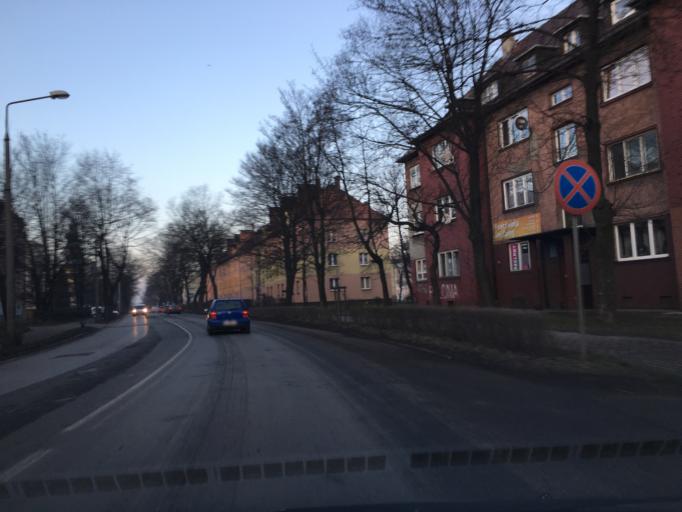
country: PL
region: Silesian Voivodeship
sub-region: Bytom
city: Bytom
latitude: 50.3481
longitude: 18.8769
